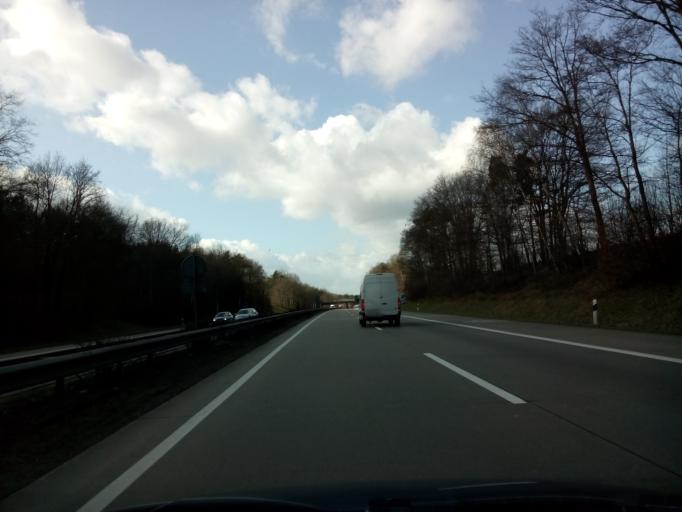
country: DE
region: Lower Saxony
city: Wildeshausen
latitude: 52.9165
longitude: 8.4594
